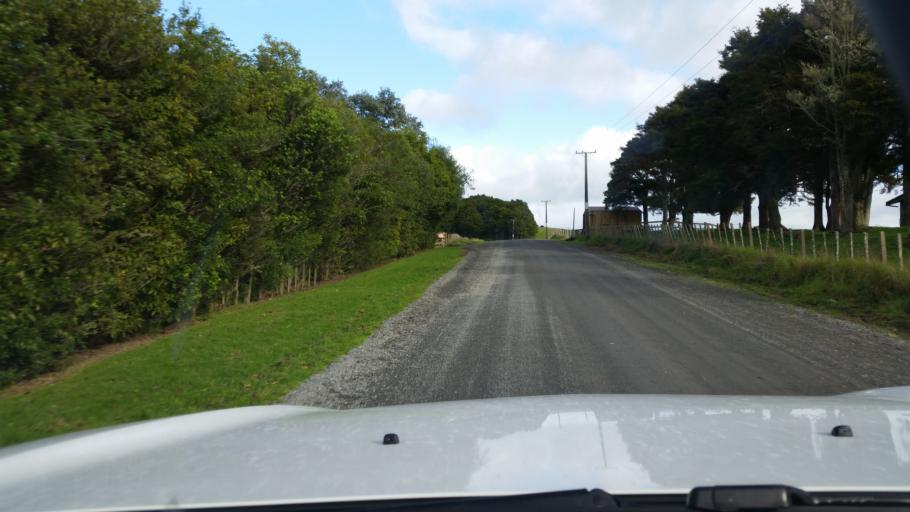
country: NZ
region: Northland
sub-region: Whangarei
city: Maungatapere
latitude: -35.6643
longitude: 174.1064
